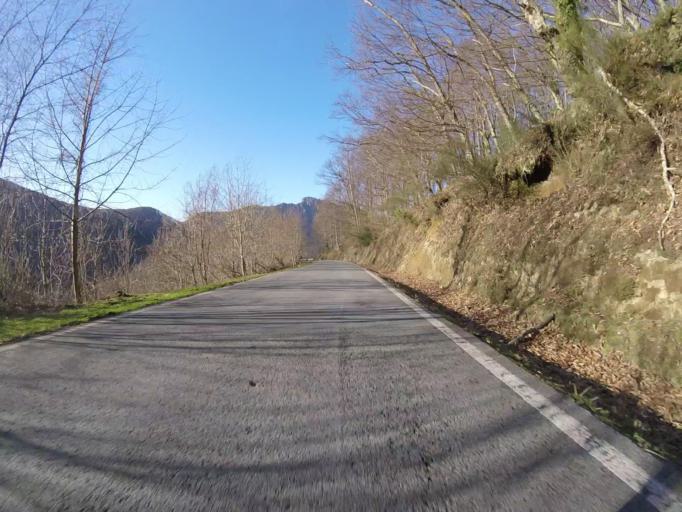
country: ES
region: Navarre
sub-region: Provincia de Navarra
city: Lesaka
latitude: 43.2621
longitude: -1.7644
